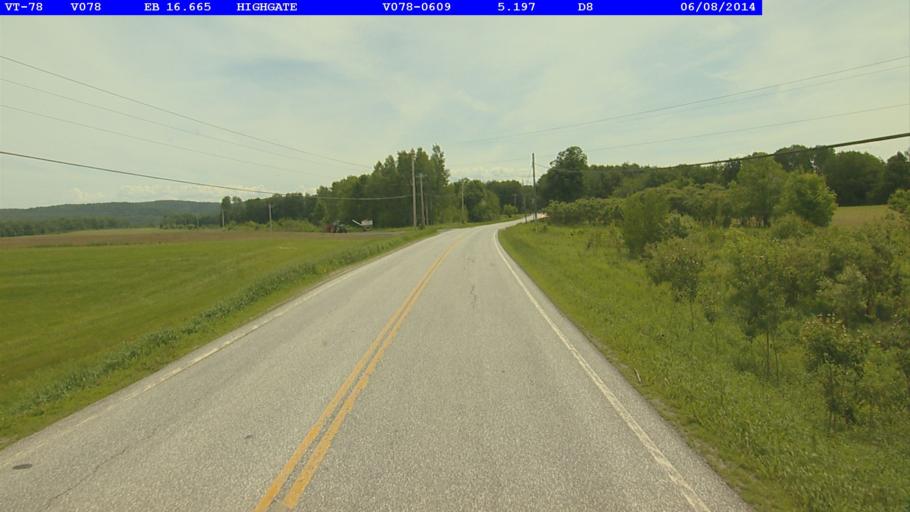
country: US
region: Vermont
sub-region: Franklin County
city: Swanton
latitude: 44.9420
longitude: -73.0070
